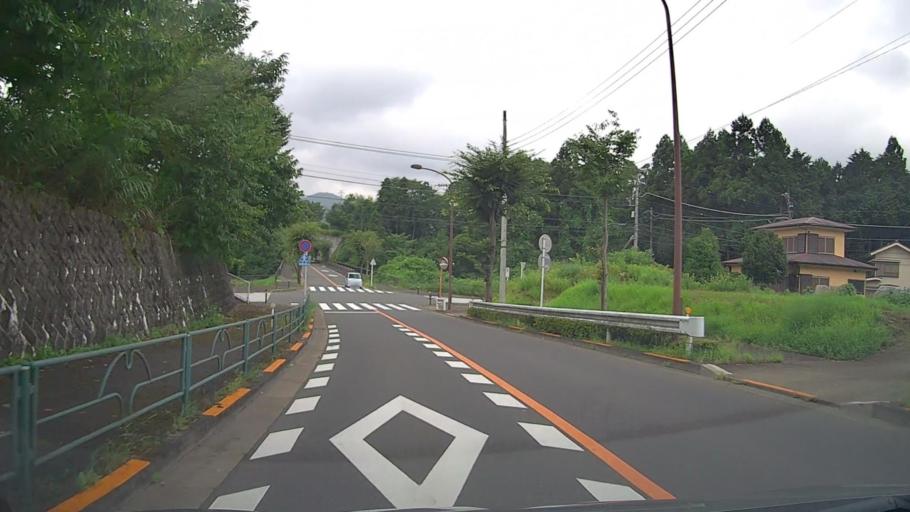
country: JP
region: Tokyo
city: Itsukaichi
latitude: 35.7228
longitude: 139.2367
